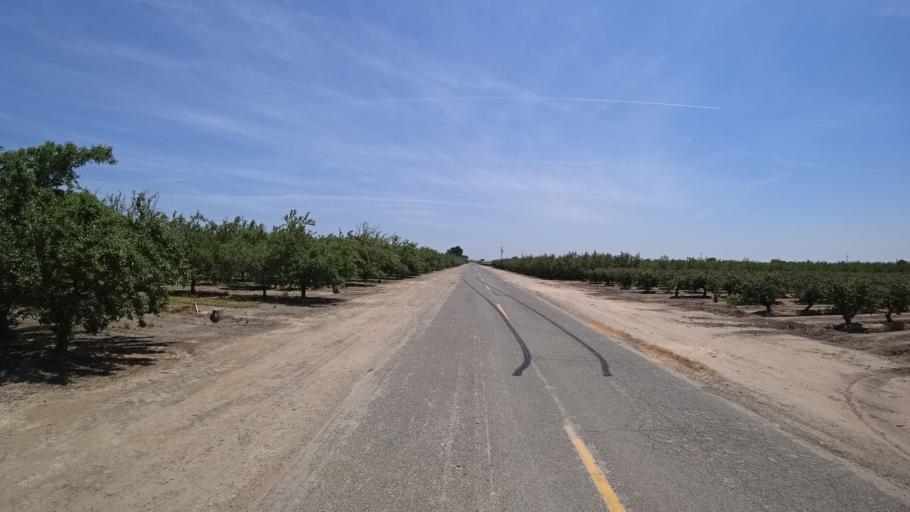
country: US
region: California
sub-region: Fresno County
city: Riverdale
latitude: 36.3875
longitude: -119.8670
